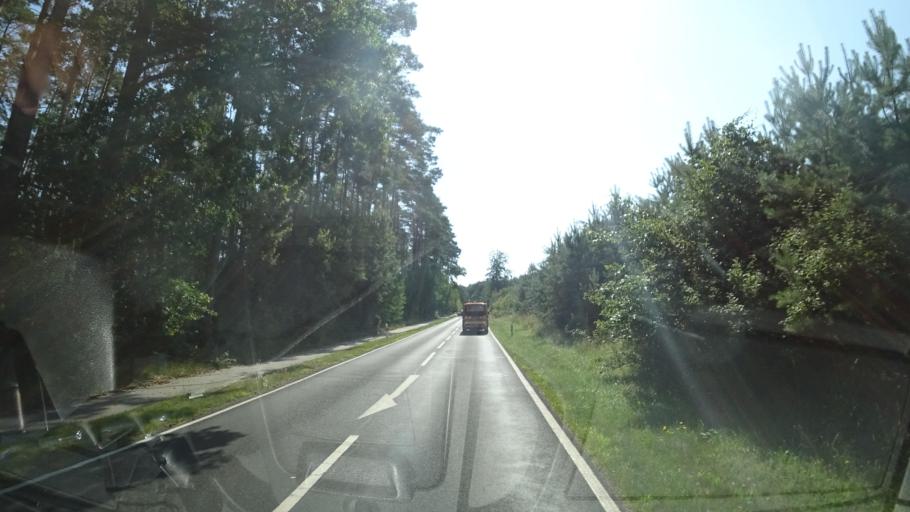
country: DE
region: Mecklenburg-Vorpommern
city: Kroslin
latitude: 54.1391
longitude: 13.7071
